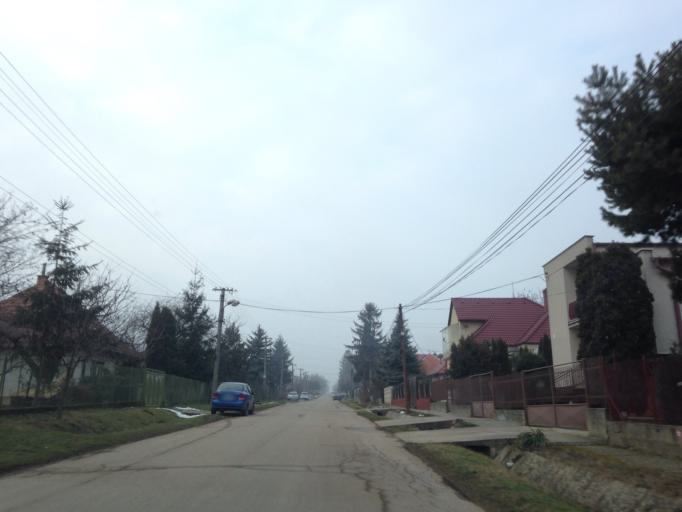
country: SK
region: Nitriansky
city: Svodin
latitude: 47.9926
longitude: 18.3908
